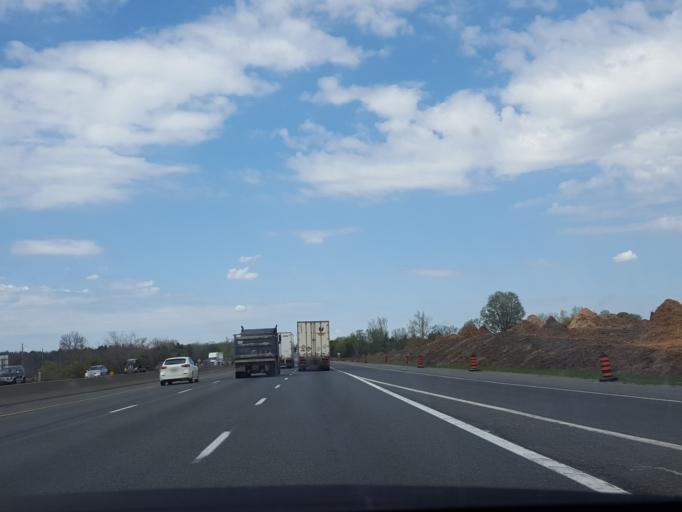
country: CA
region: Ontario
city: Oshawa
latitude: 43.8785
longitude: -78.7662
